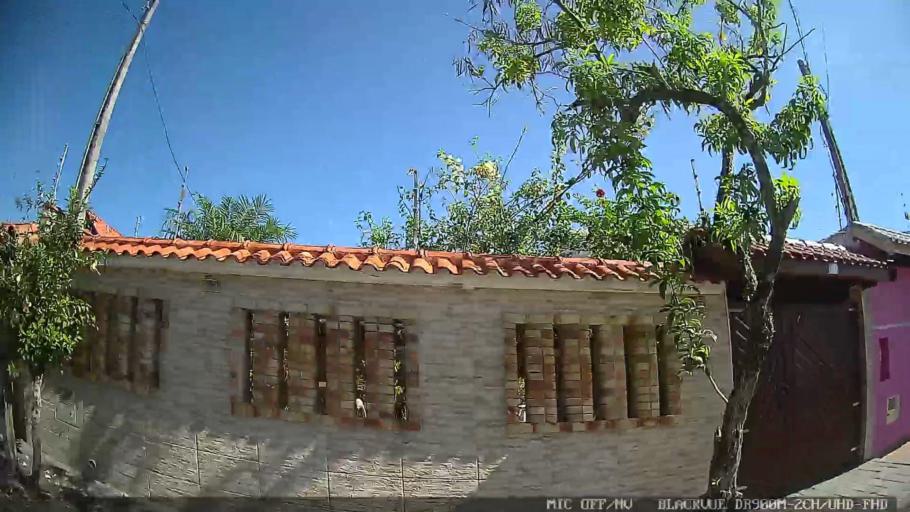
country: BR
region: Sao Paulo
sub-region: Peruibe
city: Peruibe
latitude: -24.2746
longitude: -46.9430
